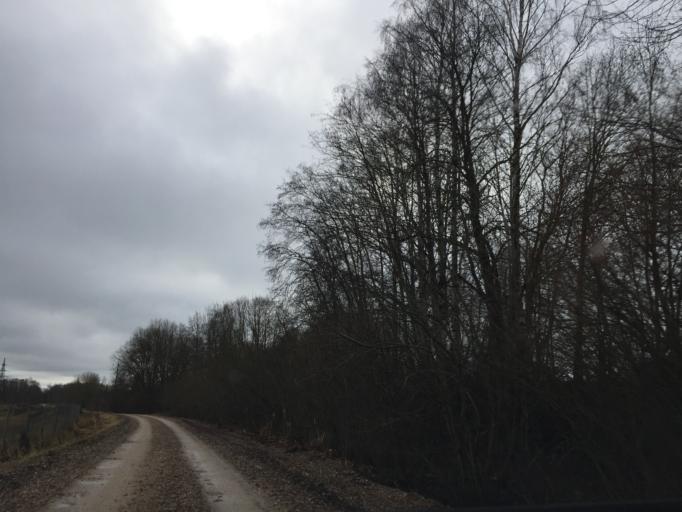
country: LV
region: Broceni
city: Broceni
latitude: 56.6779
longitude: 22.5577
